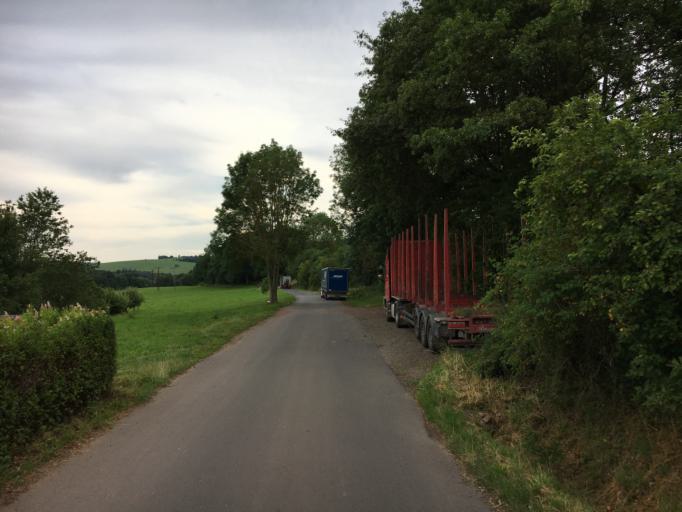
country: DE
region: Thuringia
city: Schmalkalden
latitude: 50.7522
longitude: 10.4664
